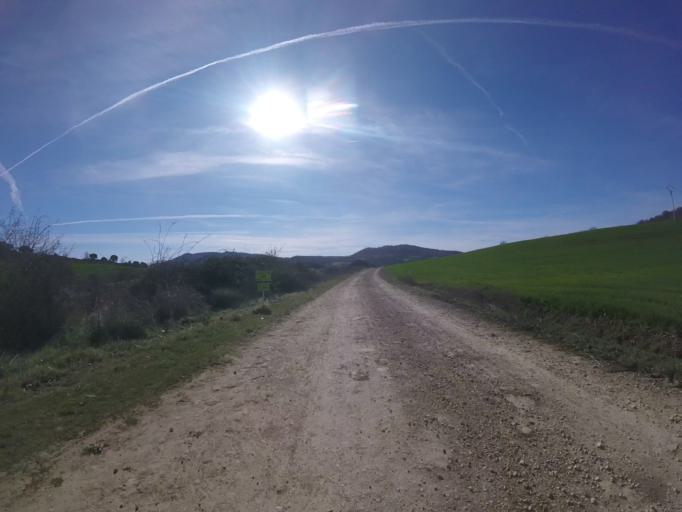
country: ES
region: Navarre
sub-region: Provincia de Navarra
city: Yerri
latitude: 42.6758
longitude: -1.9578
